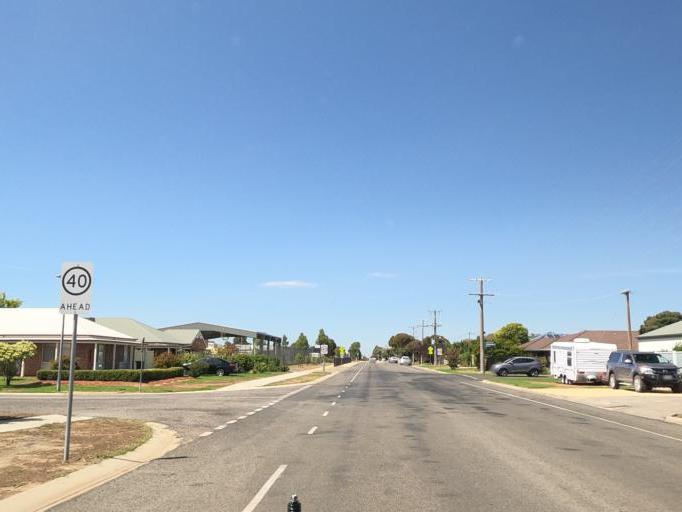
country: AU
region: Victoria
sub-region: Moira
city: Yarrawonga
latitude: -36.0105
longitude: 146.0132
